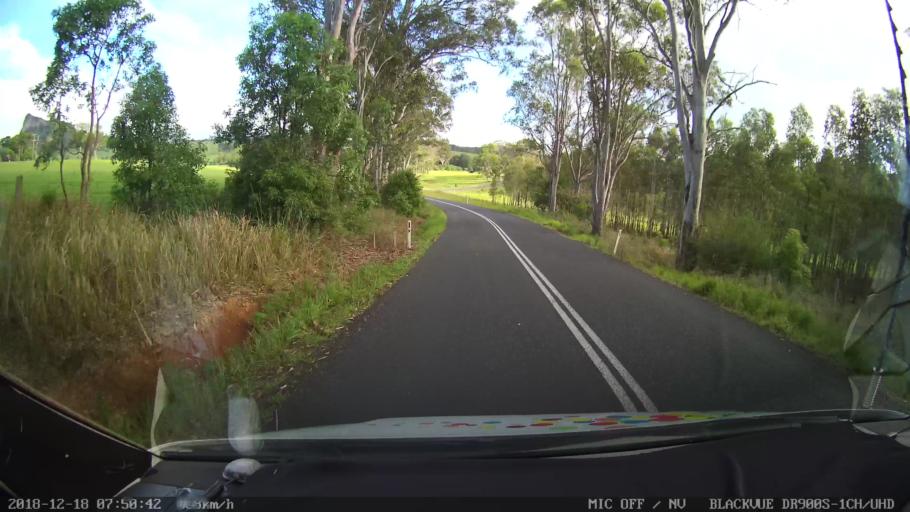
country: AU
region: New South Wales
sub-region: Kyogle
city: Kyogle
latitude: -28.4433
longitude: 152.5745
